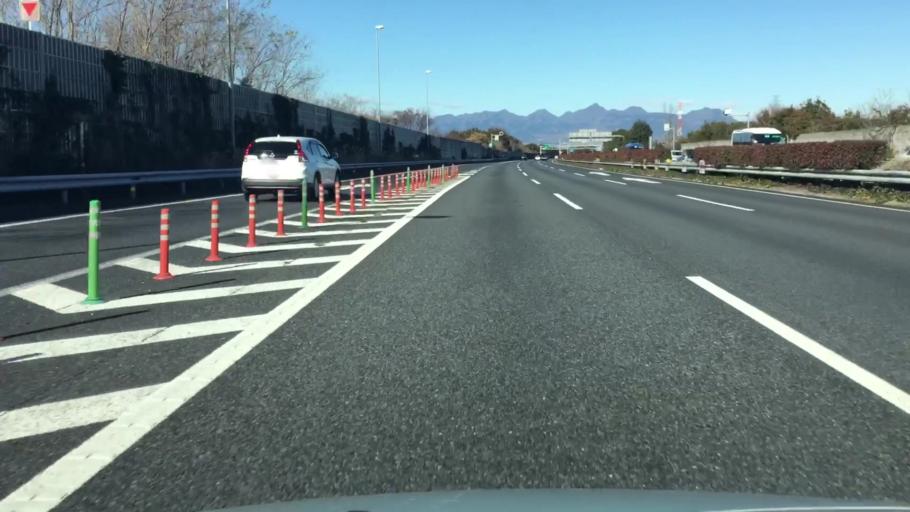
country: JP
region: Gunma
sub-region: Sawa-gun
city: Tamamura
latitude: 36.3237
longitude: 139.0710
